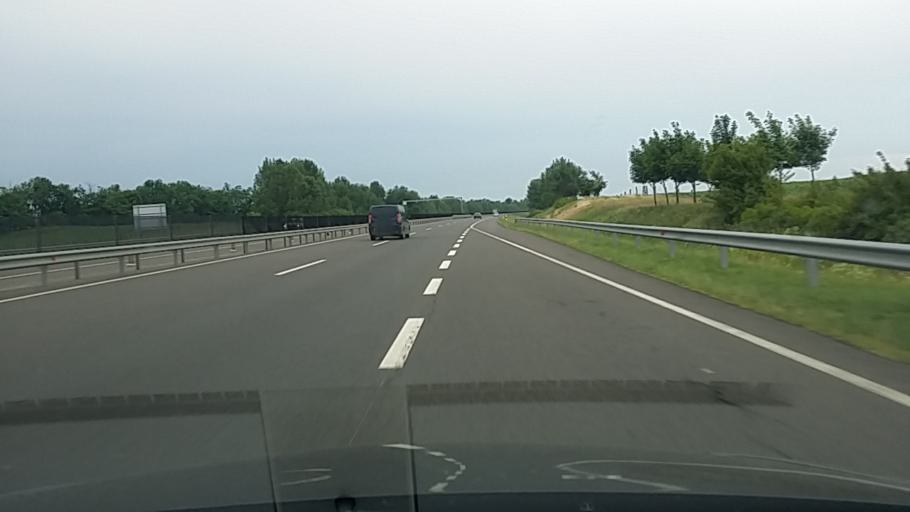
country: HU
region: Szabolcs-Szatmar-Bereg
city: Kalmanhaza
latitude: 47.8999
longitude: 21.5517
